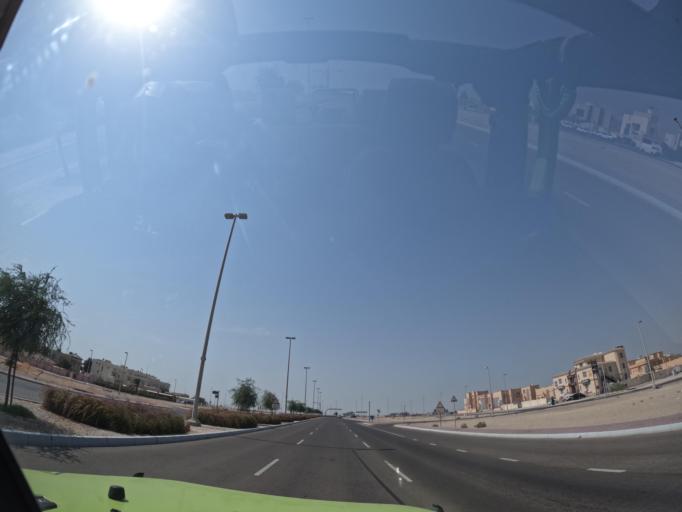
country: AE
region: Abu Dhabi
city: Abu Dhabi
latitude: 24.3556
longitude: 54.6150
